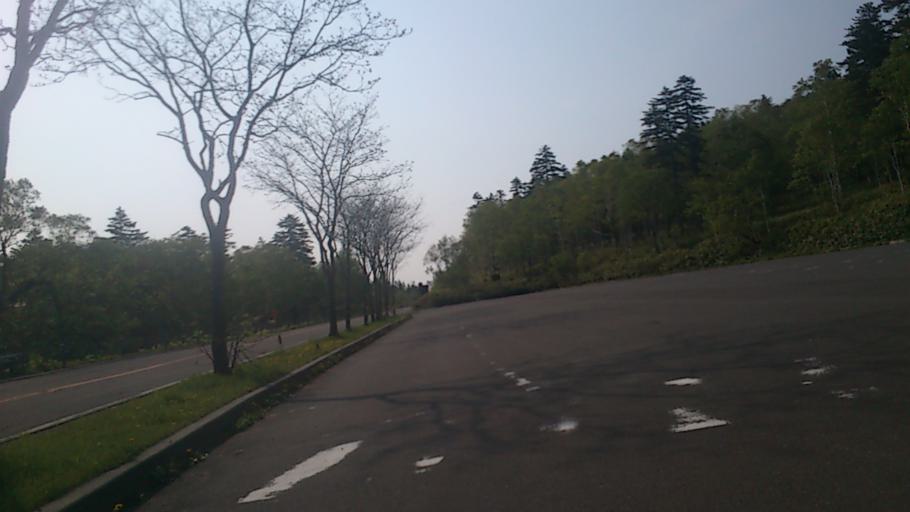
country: JP
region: Hokkaido
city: Bihoro
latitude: 43.4487
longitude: 144.2044
